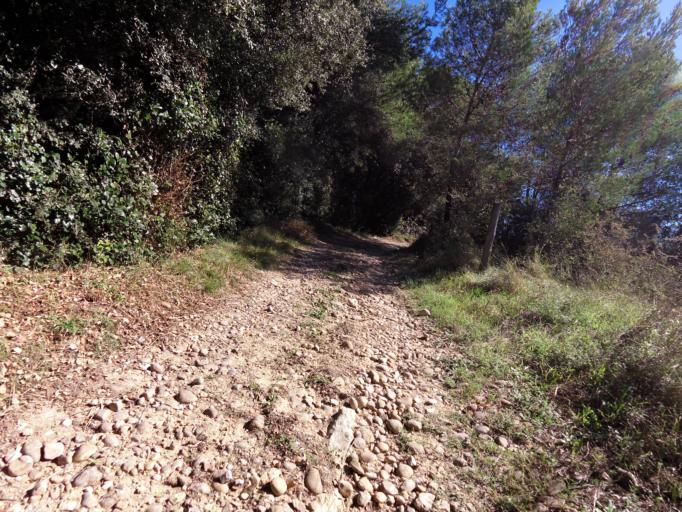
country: FR
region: Languedoc-Roussillon
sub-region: Departement du Gard
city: Aigues-Vives
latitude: 43.7352
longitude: 4.1906
